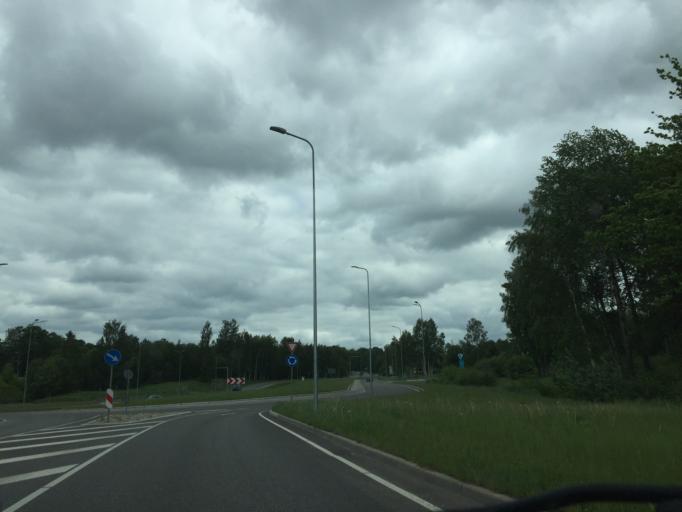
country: LV
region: Valmieras Rajons
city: Valmiera
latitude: 57.5263
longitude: 25.4490
